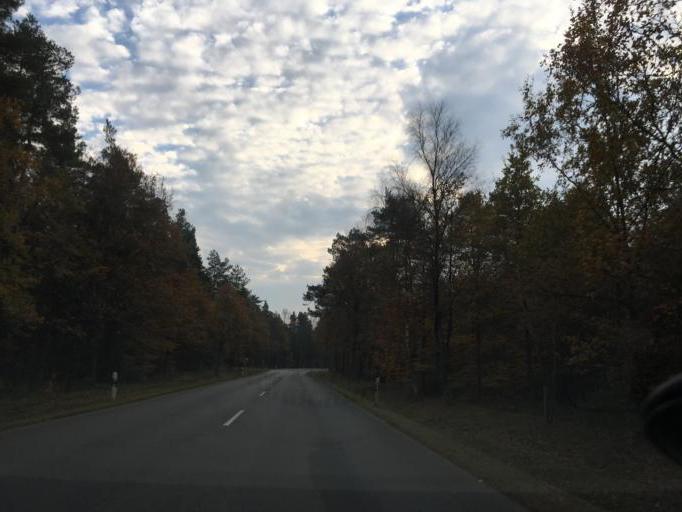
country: DE
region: Lower Saxony
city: Wietzendorf
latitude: 52.9899
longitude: 9.9926
